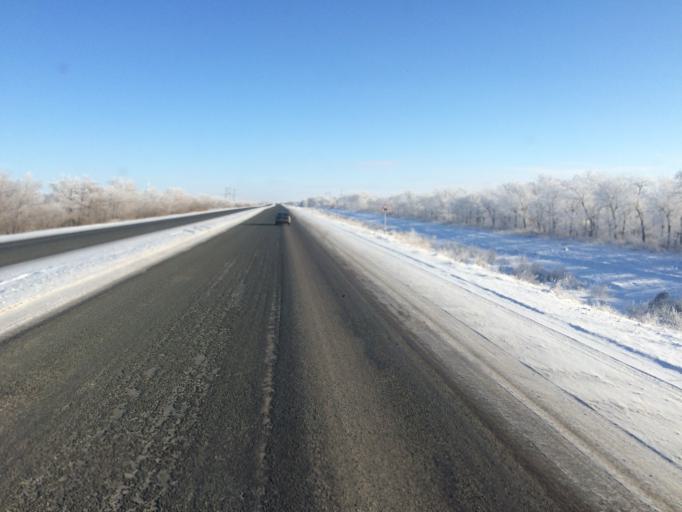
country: KZ
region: Aqtoebe
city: Aqtobe
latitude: 50.2939
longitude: 57.4976
